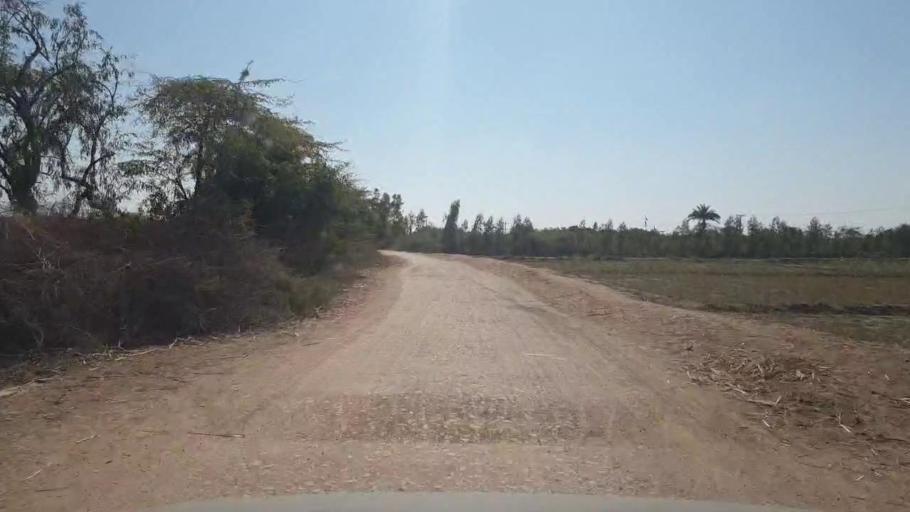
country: PK
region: Sindh
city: Mirwah Gorchani
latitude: 25.3000
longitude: 69.1310
